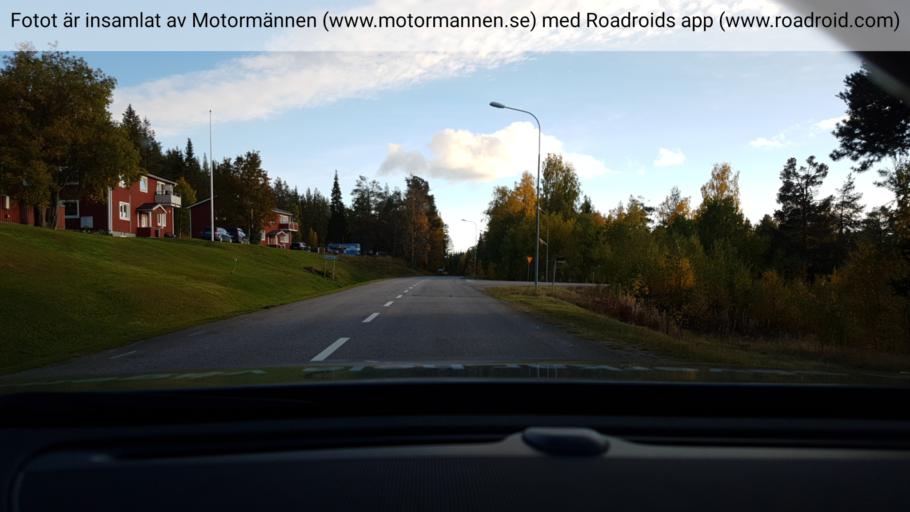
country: SE
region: Norrbotten
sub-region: Jokkmokks Kommun
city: Jokkmokk
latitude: 66.9502
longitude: 19.7961
